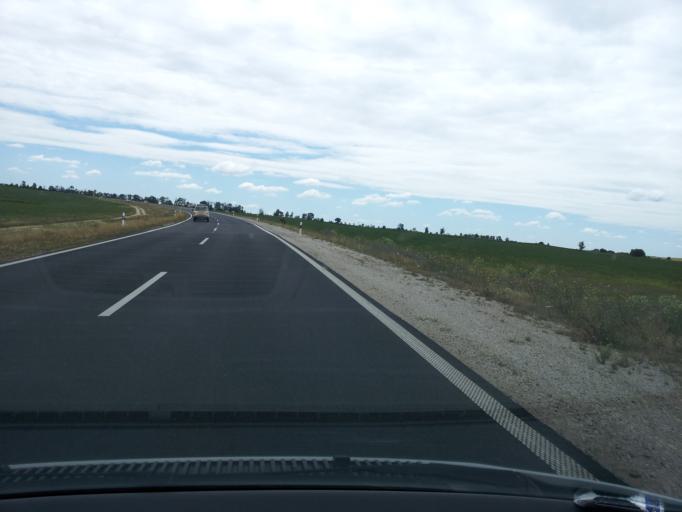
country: HU
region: Veszprem
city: Balatonkenese
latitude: 47.0667
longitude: 18.0796
